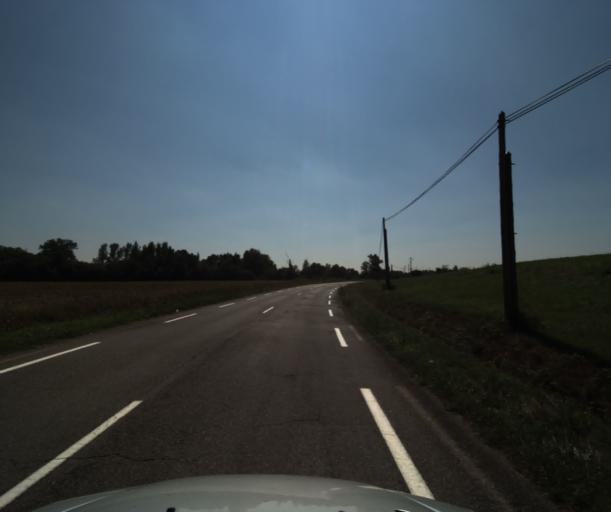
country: FR
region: Midi-Pyrenees
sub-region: Departement de la Haute-Garonne
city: Labastidette
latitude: 43.4513
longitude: 1.2808
